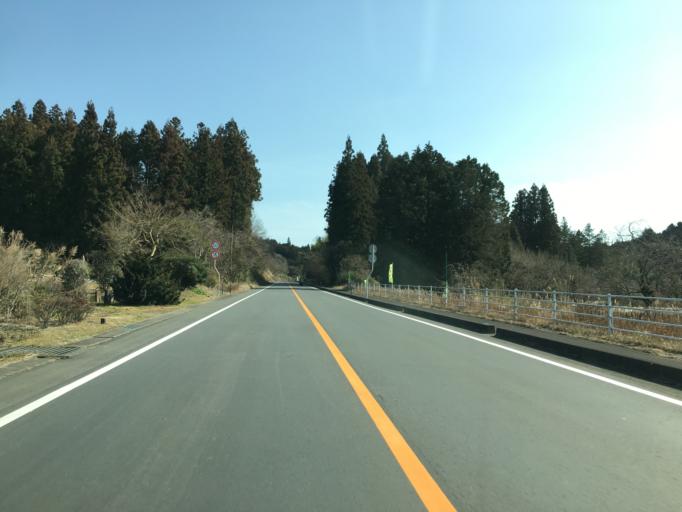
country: JP
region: Ibaraki
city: Daigo
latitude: 36.8117
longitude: 140.4659
